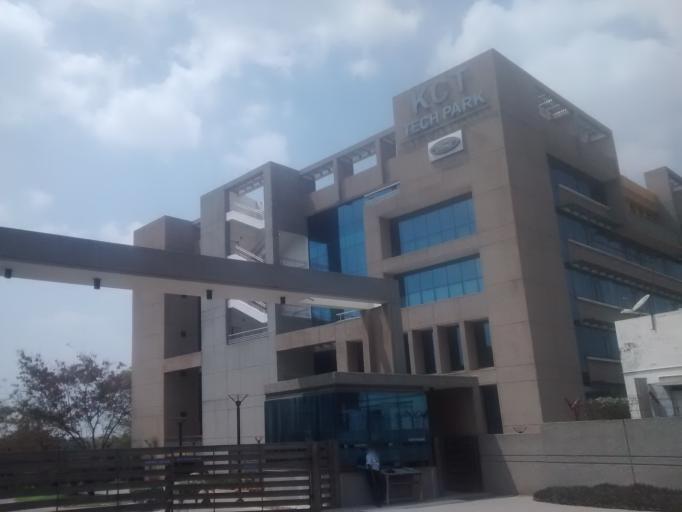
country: IN
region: Tamil Nadu
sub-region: Coimbatore
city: Coimbatore
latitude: 11.0815
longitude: 76.9895
